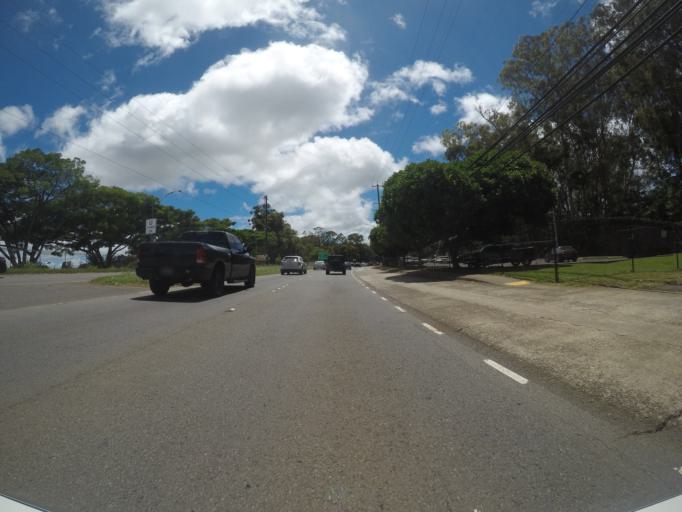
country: US
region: Hawaii
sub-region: Honolulu County
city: Wahiawa
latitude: 21.4889
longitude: -158.0375
